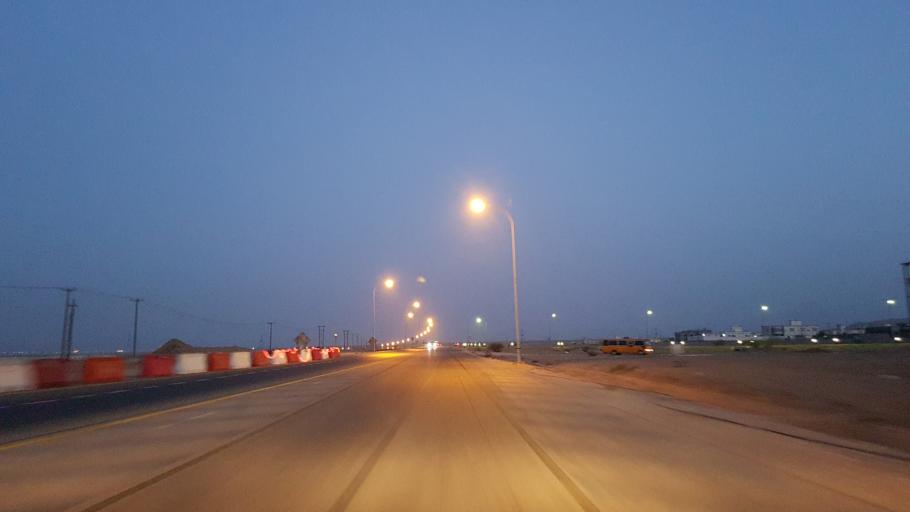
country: OM
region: Ash Sharqiyah
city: Sur
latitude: 22.5953
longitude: 59.4360
